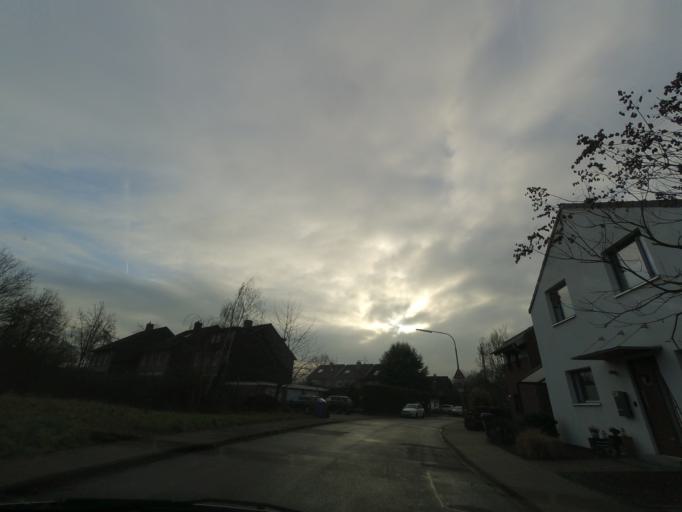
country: DE
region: North Rhine-Westphalia
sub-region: Regierungsbezirk Dusseldorf
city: Neubrueck
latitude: 51.1625
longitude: 6.5776
